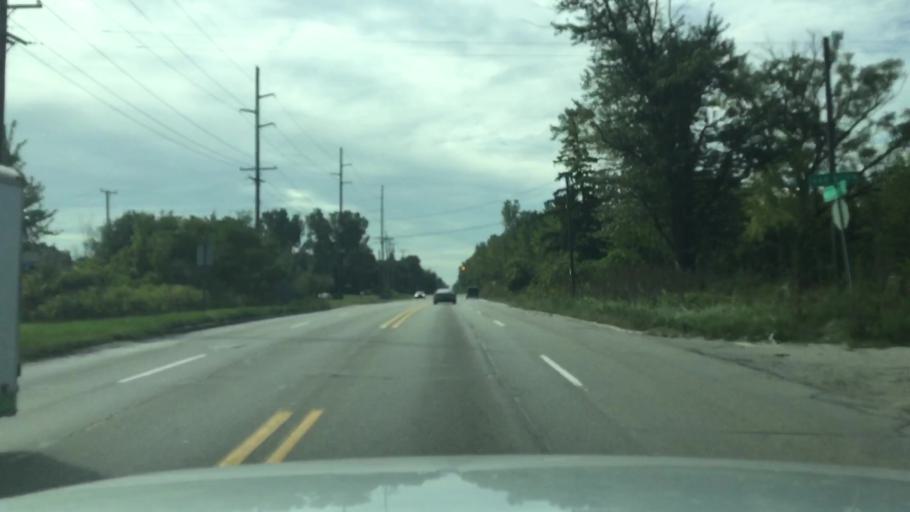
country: US
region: Michigan
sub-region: Wayne County
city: Canton
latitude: 42.2600
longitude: -83.4868
